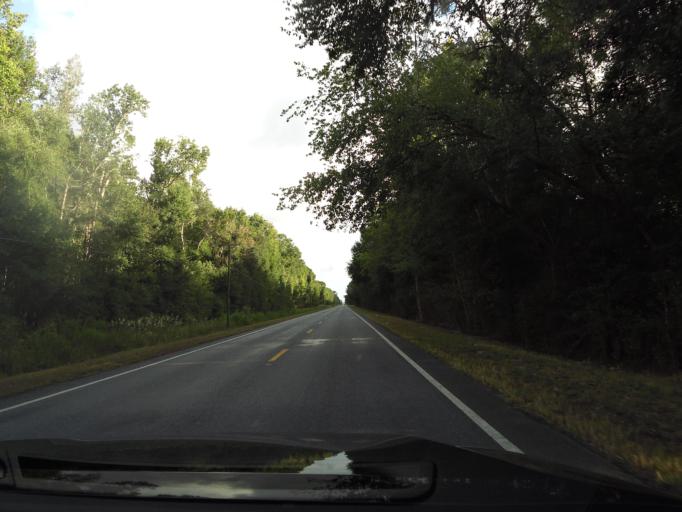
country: US
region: Georgia
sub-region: Liberty County
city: Midway
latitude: 31.6906
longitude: -81.4091
